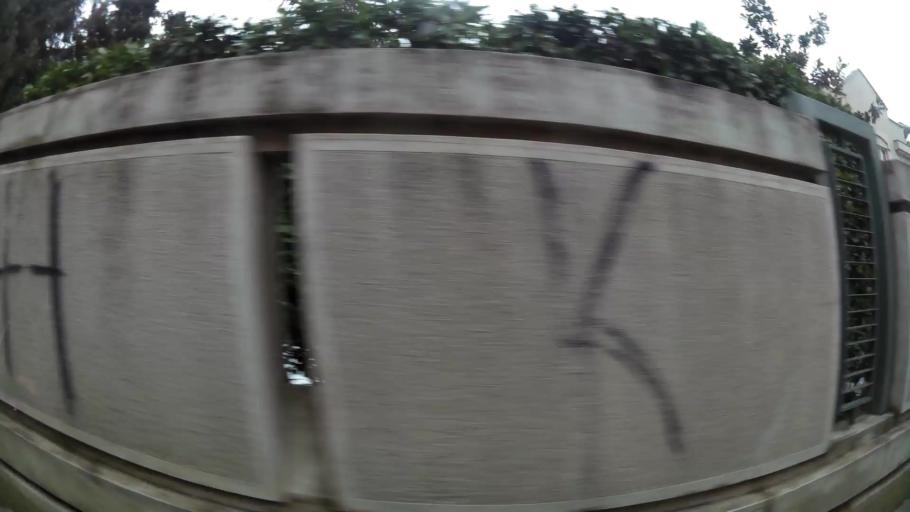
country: RS
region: Central Serbia
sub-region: Belgrade
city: Vozdovac
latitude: 44.7617
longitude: 20.5017
